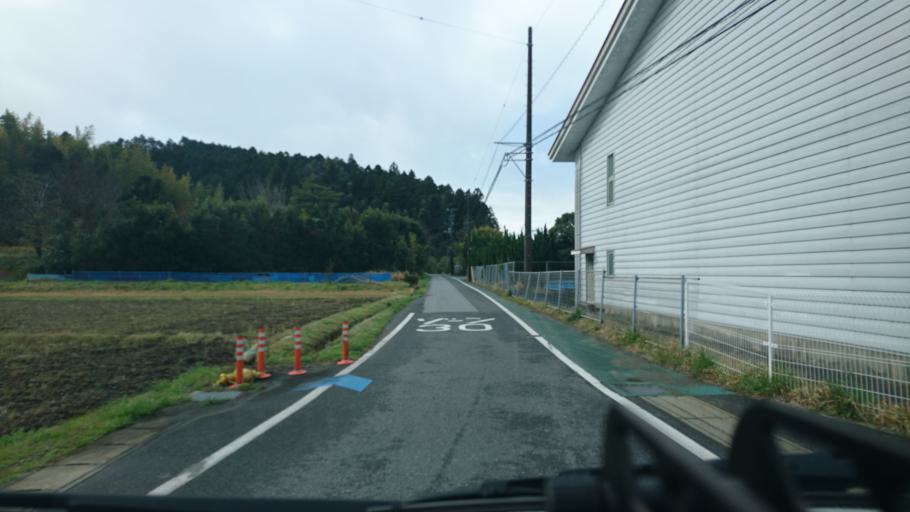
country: JP
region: Chiba
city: Kimitsu
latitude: 35.3042
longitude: 139.9596
